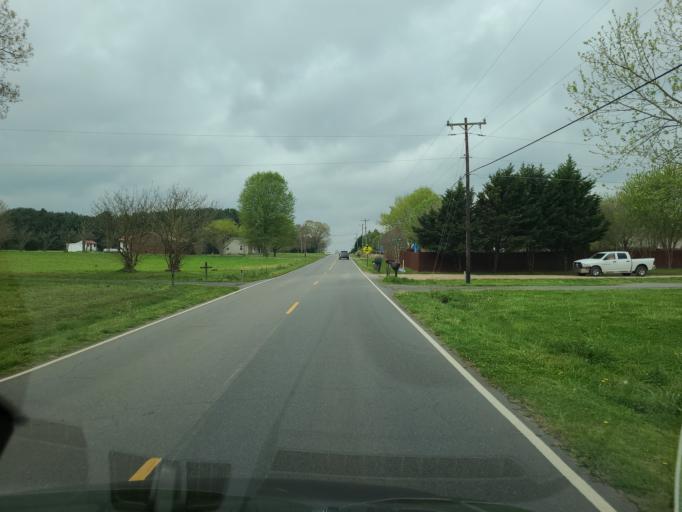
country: US
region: North Carolina
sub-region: Lincoln County
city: Lincolnton
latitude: 35.4570
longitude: -81.3052
